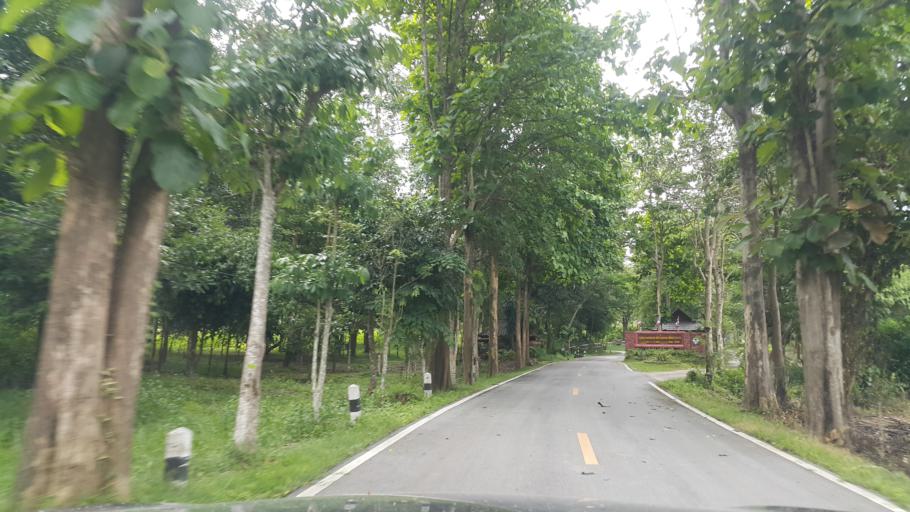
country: TH
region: Phitsanulok
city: Chat Trakan
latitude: 17.3016
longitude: 100.6758
